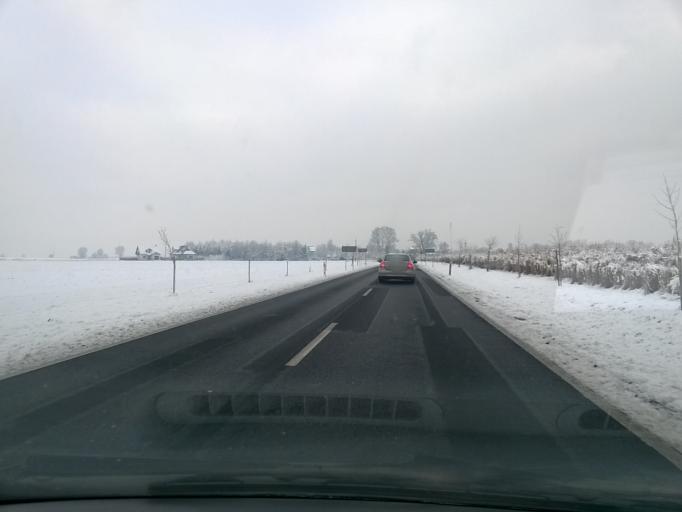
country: PL
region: Kujawsko-Pomorskie
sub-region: Powiat bydgoski
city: Koronowo
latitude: 53.3252
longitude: 17.9114
